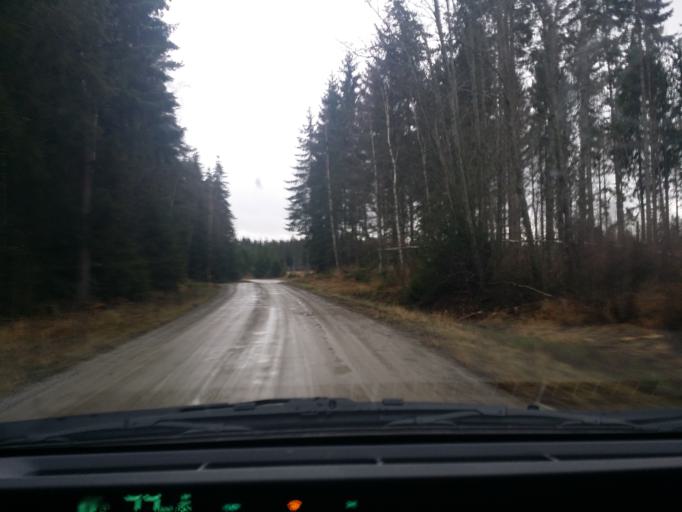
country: SE
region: Vaestmanland
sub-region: Surahammars Kommun
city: Surahammar
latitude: 59.7652
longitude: 16.2951
